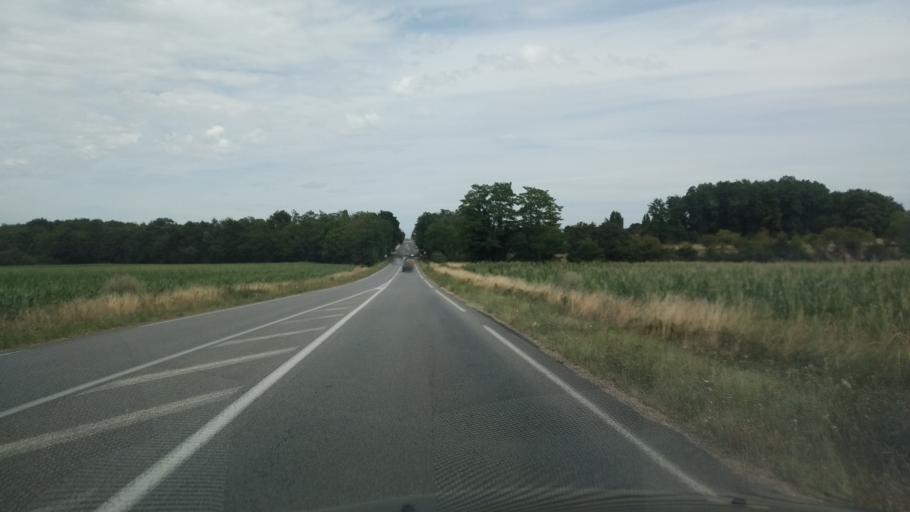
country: FR
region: Poitou-Charentes
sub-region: Departement de la Vienne
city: Mignaloux-Beauvoir
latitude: 46.5622
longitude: 0.4230
